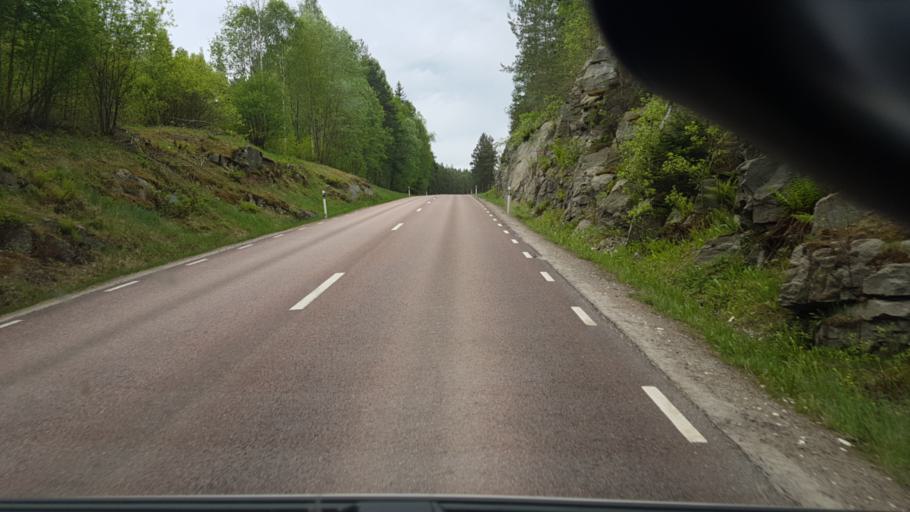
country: SE
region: Vaermland
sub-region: Arvika Kommun
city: Arvika
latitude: 59.6341
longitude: 12.6177
